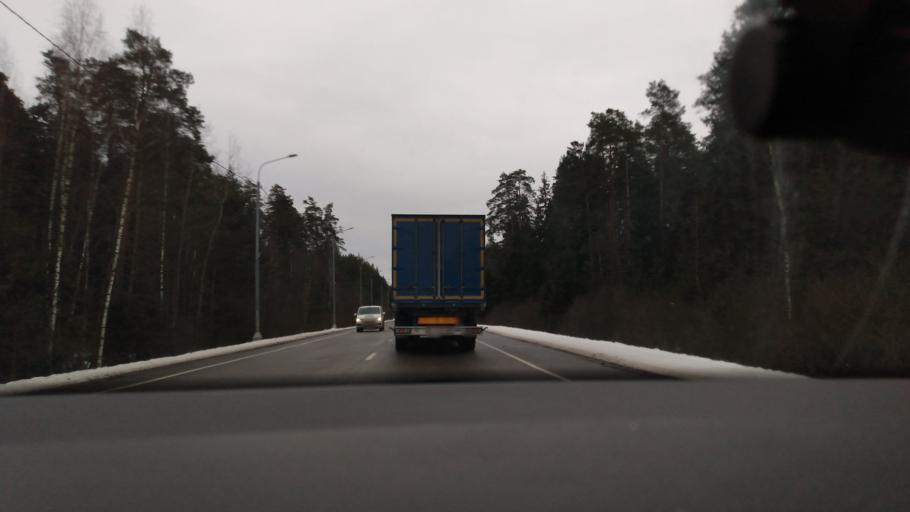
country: RU
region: Moskovskaya
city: Yegor'yevsk
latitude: 55.4553
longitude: 38.9943
